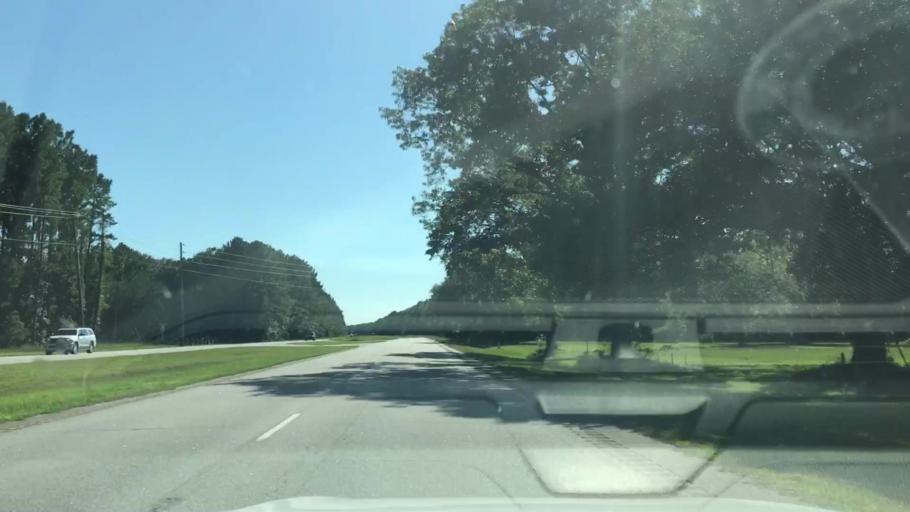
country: US
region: South Carolina
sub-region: Charleston County
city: Awendaw
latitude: 32.9823
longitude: -79.6581
